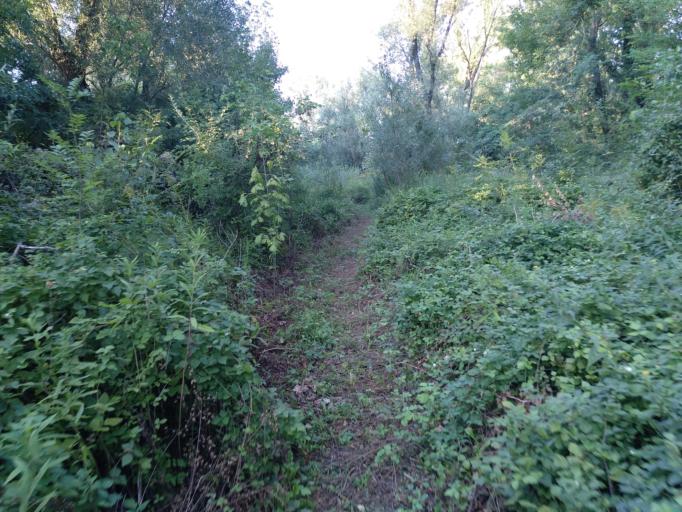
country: FR
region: Rhone-Alpes
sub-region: Departement du Rhone
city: Grigny
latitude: 45.5989
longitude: 4.7929
